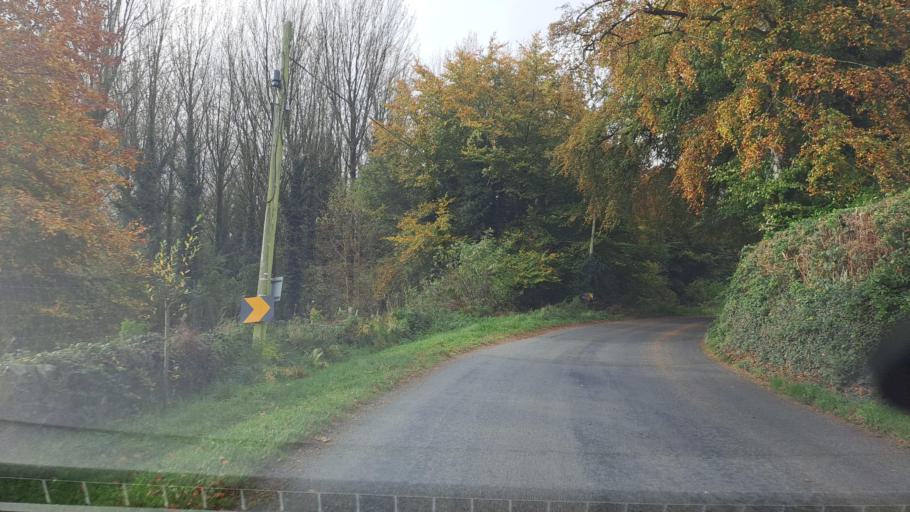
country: IE
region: Ulster
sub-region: An Cabhan
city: Bailieborough
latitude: 54.0482
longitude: -6.9064
